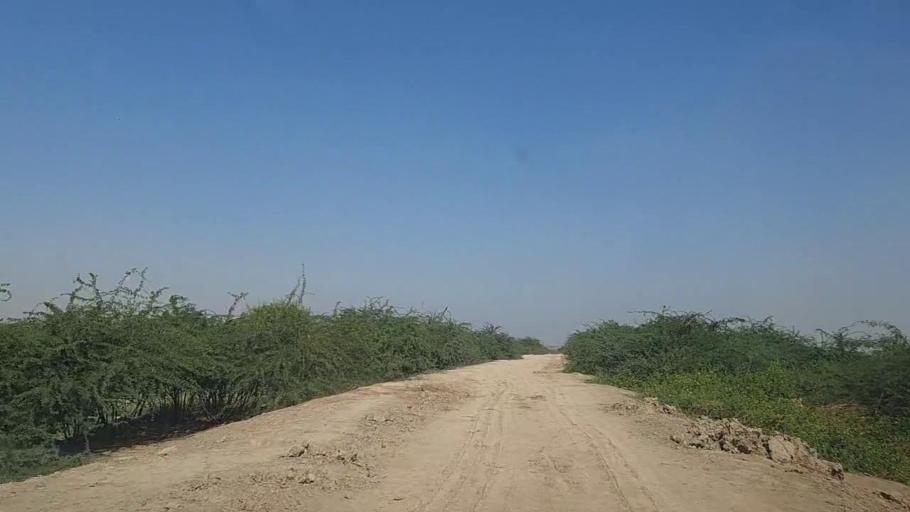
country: PK
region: Sindh
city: Thatta
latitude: 24.8403
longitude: 68.0212
